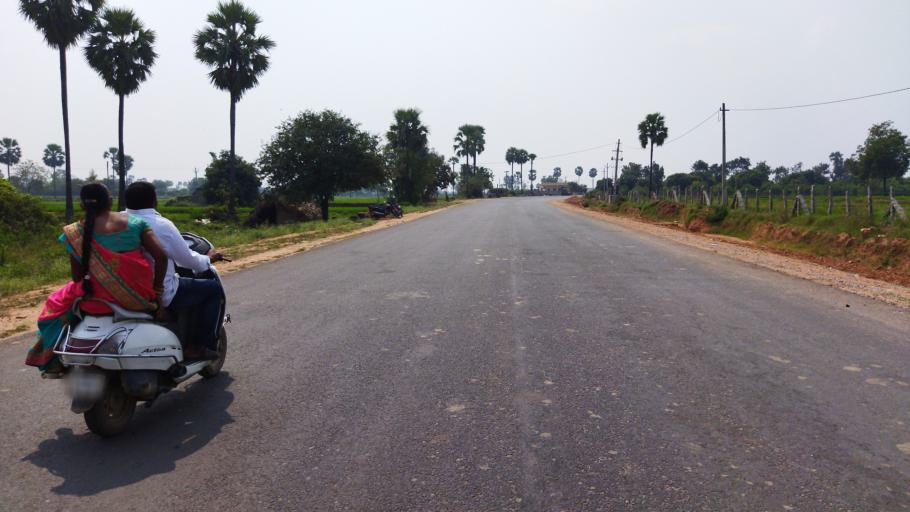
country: IN
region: Telangana
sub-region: Nalgonda
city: Nalgonda
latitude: 17.1134
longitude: 79.3603
